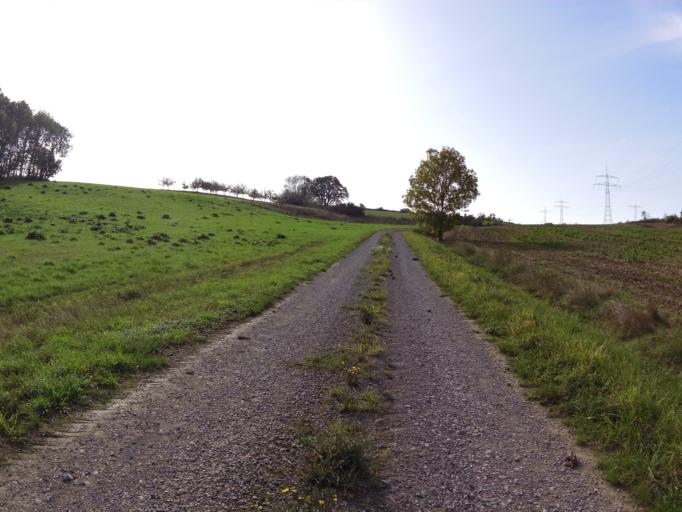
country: DE
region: Bavaria
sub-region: Regierungsbezirk Unterfranken
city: Theilheim
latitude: 49.7552
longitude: 10.0580
